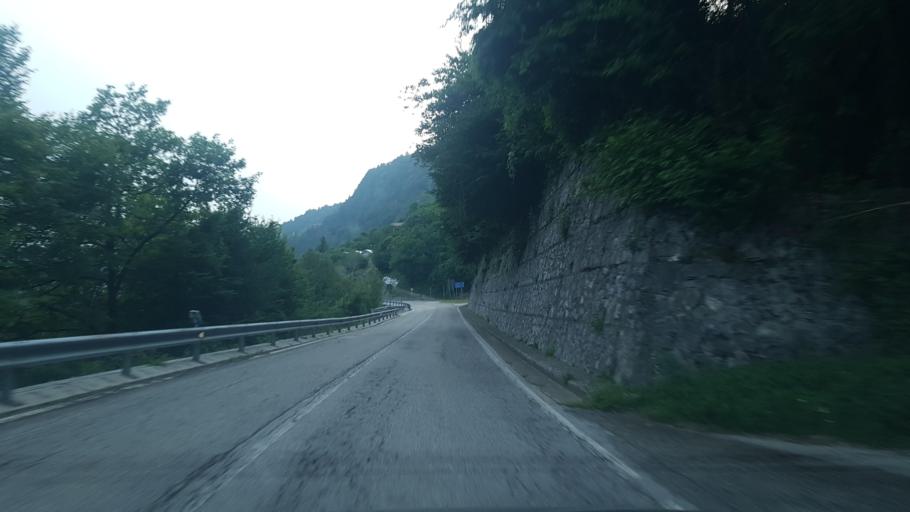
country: IT
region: Friuli Venezia Giulia
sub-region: Provincia di Udine
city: Paularo
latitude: 46.4899
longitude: 13.1006
